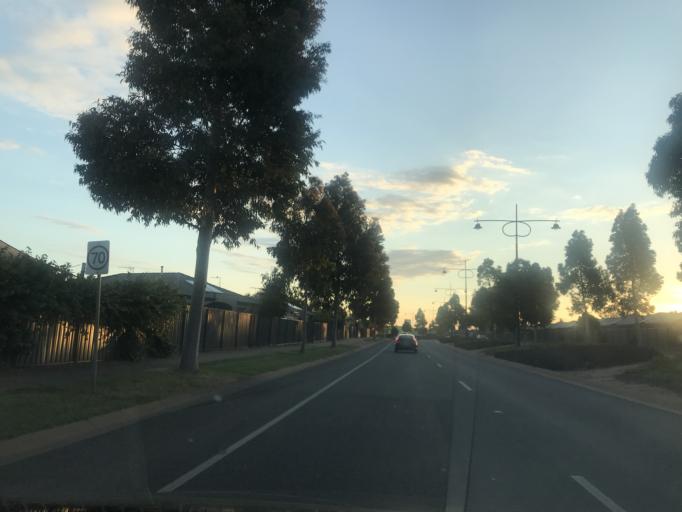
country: AU
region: Victoria
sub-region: Wyndham
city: Point Cook
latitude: -37.8911
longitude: 144.7315
